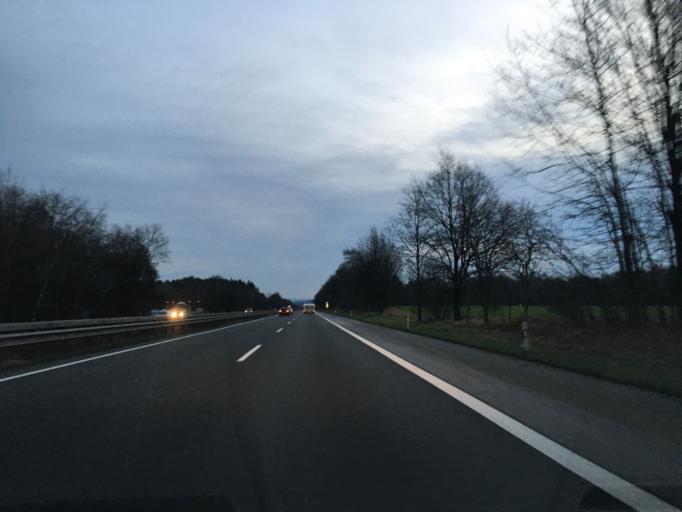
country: DE
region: Lower Saxony
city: Seevetal
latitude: 53.3771
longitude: 9.9476
